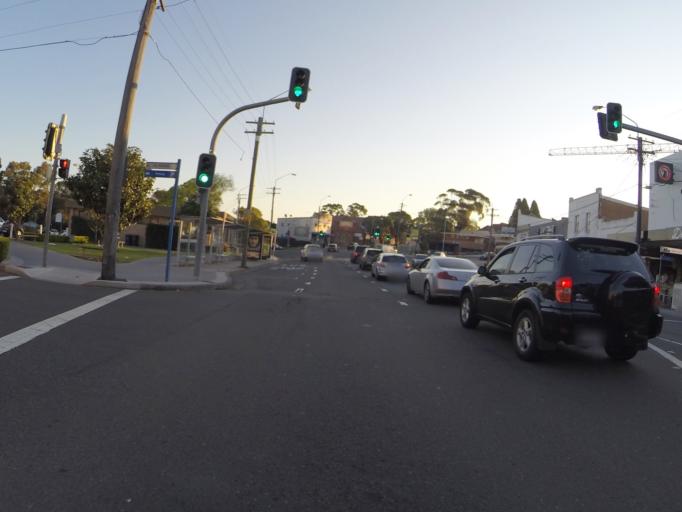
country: AU
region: New South Wales
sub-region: Rockdale
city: Bardwell Valley
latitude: -33.9269
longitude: 151.1250
